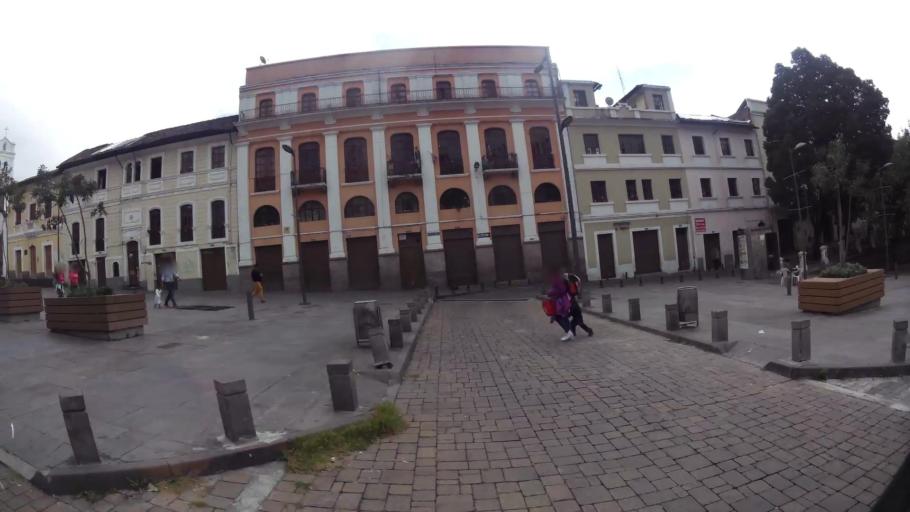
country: EC
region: Pichincha
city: Quito
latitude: -0.2226
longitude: -78.5173
